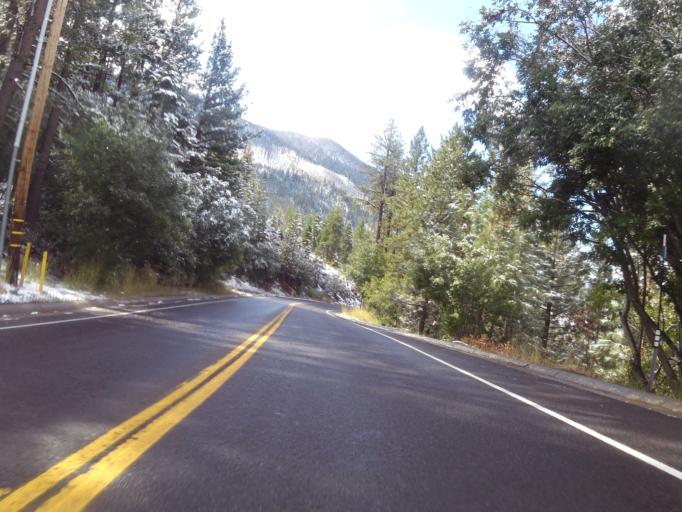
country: US
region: Nevada
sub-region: Douglas County
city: Kingsbury
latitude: 38.9688
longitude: -119.9174
